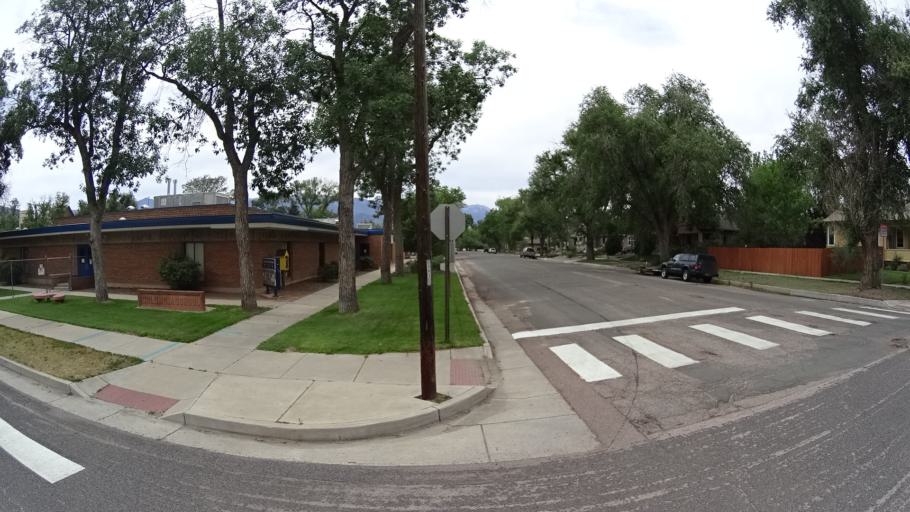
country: US
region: Colorado
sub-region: El Paso County
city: Colorado Springs
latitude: 38.8404
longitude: -104.8080
